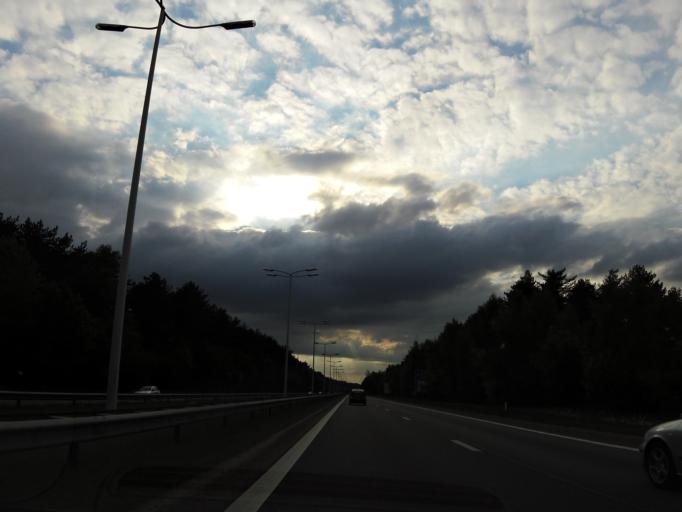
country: BE
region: Flanders
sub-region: Provincie Limburg
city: As
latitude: 50.9735
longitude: 5.5637
